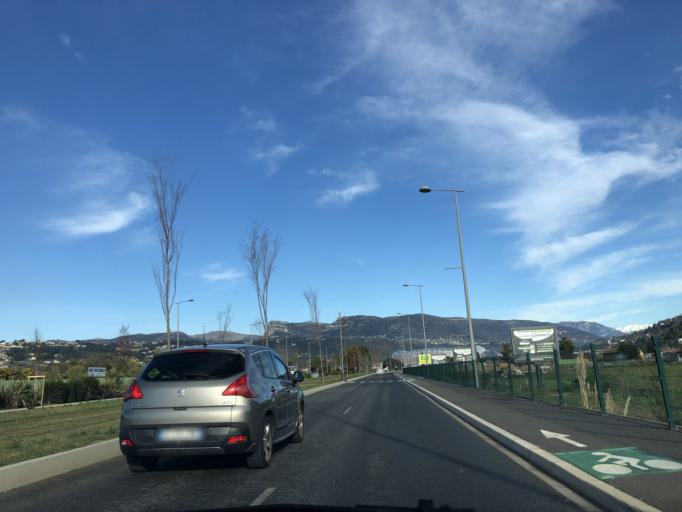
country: FR
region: Provence-Alpes-Cote d'Azur
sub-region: Departement des Alpes-Maritimes
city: Saint-Laurent-du-Var
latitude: 43.6944
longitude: 7.1985
